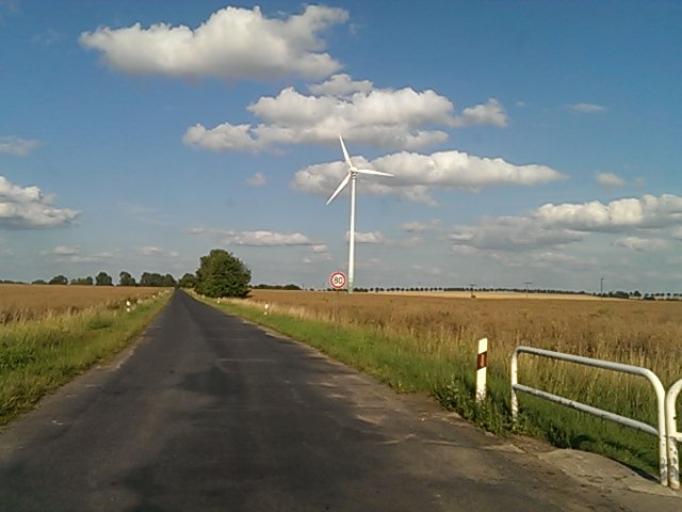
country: DE
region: Brandenburg
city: Niemegk
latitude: 52.0230
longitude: 12.6650
